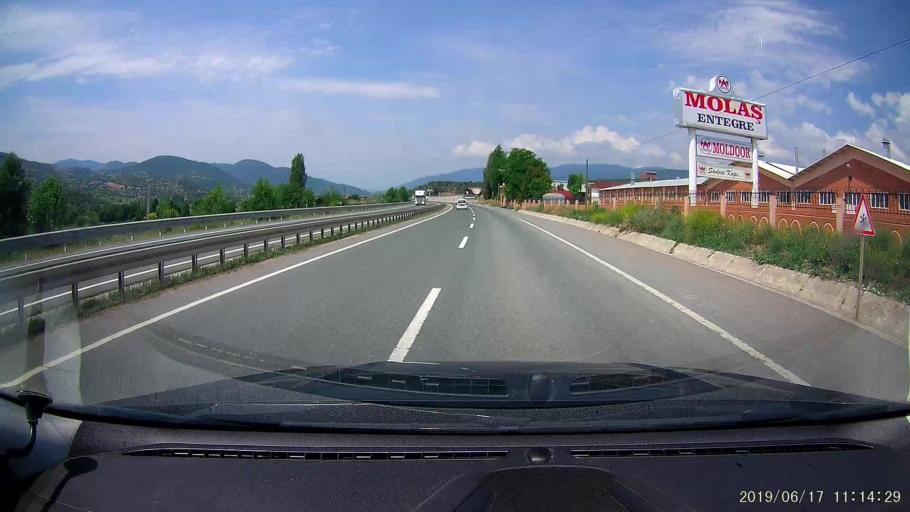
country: TR
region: Kastamonu
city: Tosya
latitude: 40.9576
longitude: 33.9465
